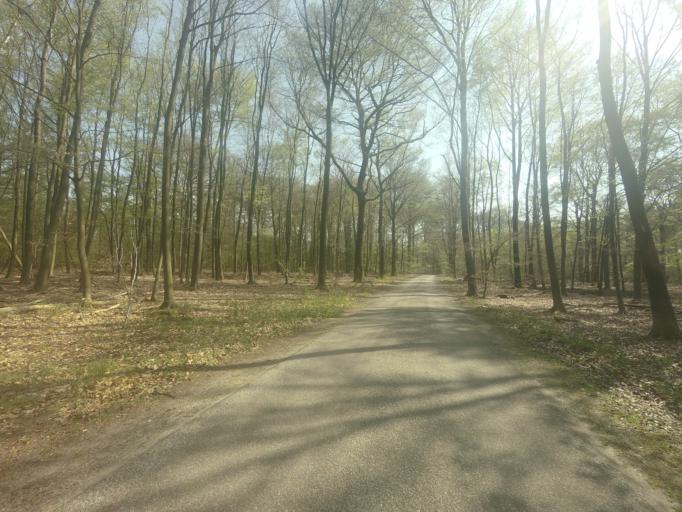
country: NL
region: North Holland
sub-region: Gemeente Hilversum
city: Hilversum
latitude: 52.1981
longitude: 5.2154
